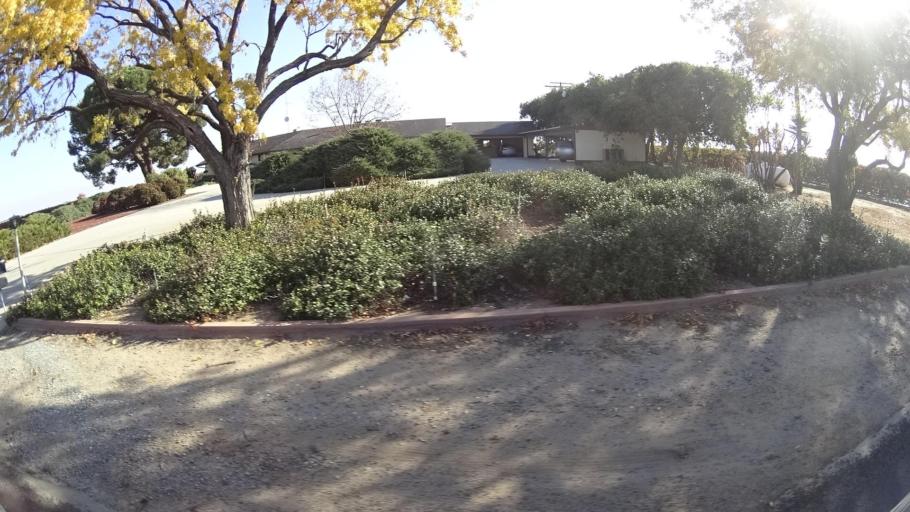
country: US
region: California
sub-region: Tulare County
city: Richgrove
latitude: 35.7416
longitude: -119.1342
